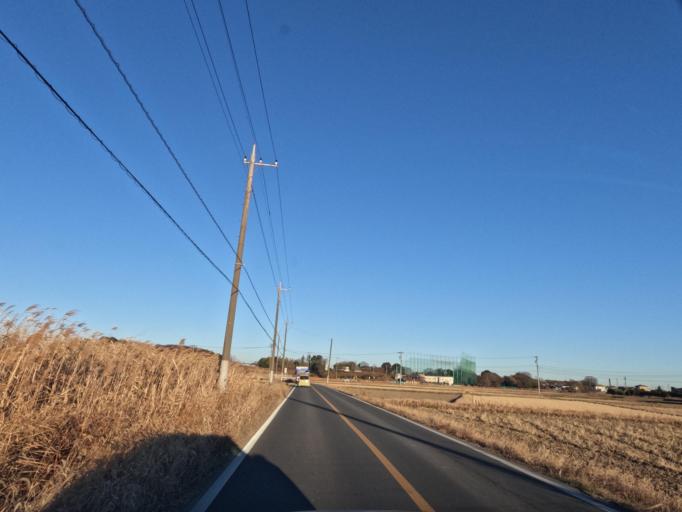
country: JP
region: Saitama
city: Hasuda
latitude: 35.9651
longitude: 139.6554
